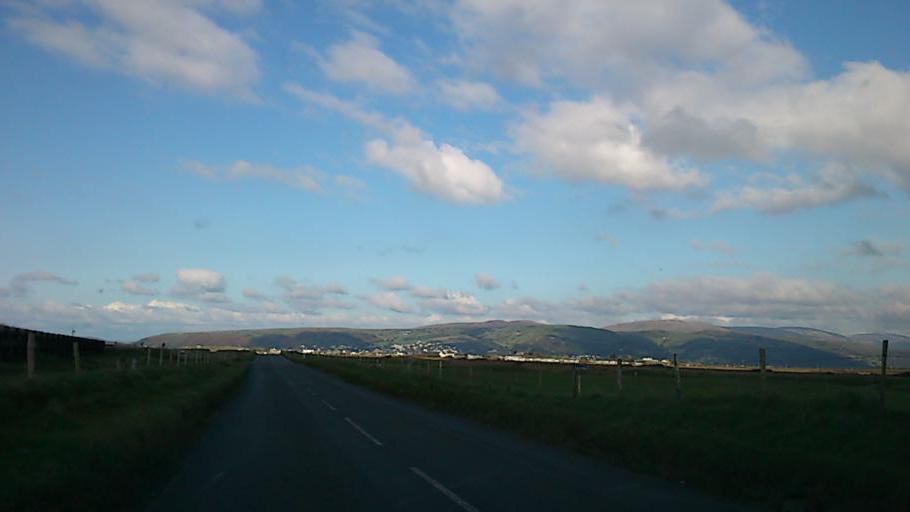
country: GB
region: Wales
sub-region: County of Ceredigion
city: Bow Street
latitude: 52.4988
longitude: -4.0522
